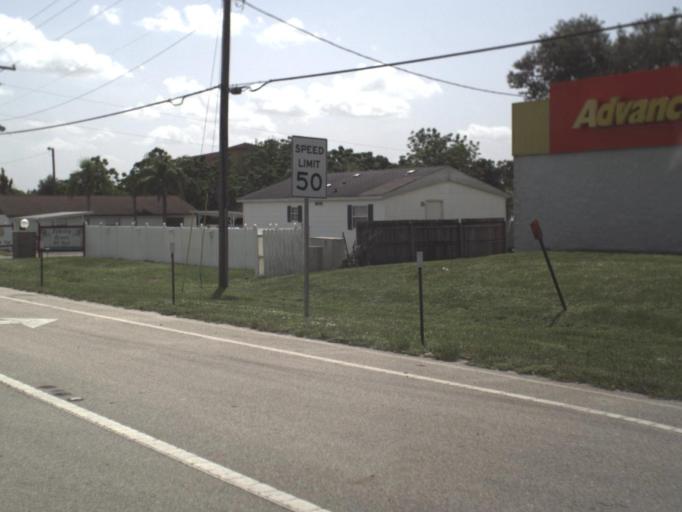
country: US
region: Florida
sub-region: Highlands County
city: Sebring
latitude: 27.4624
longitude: -81.4321
